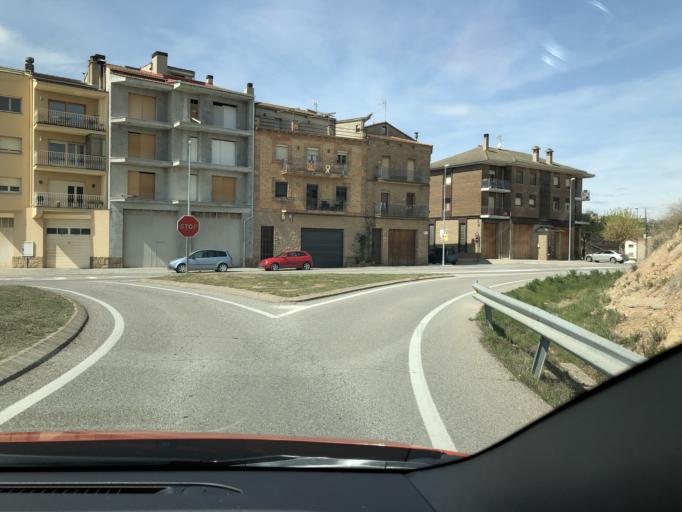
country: ES
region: Catalonia
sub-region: Provincia de Lleida
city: Solsona
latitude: 41.9984
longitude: 1.5217
